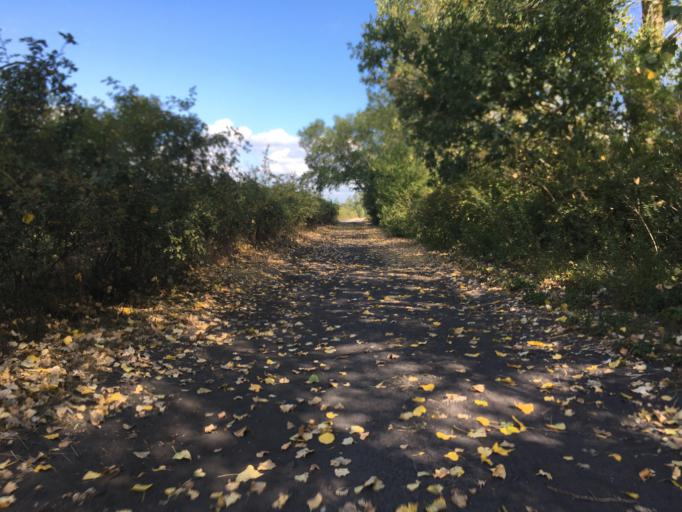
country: DE
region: Brandenburg
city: Zehdenick
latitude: 52.9758
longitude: 13.3819
